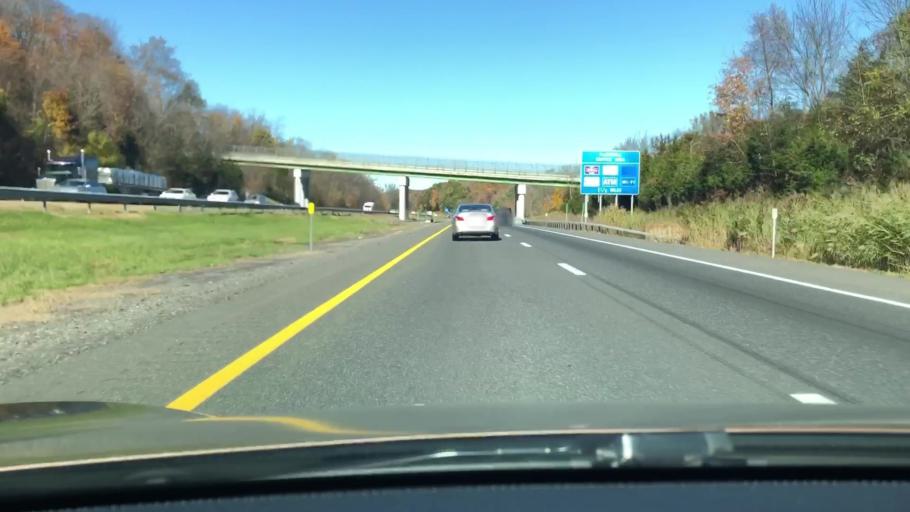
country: US
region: New York
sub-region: Orange County
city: Gardnertown
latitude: 41.5524
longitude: -74.0805
